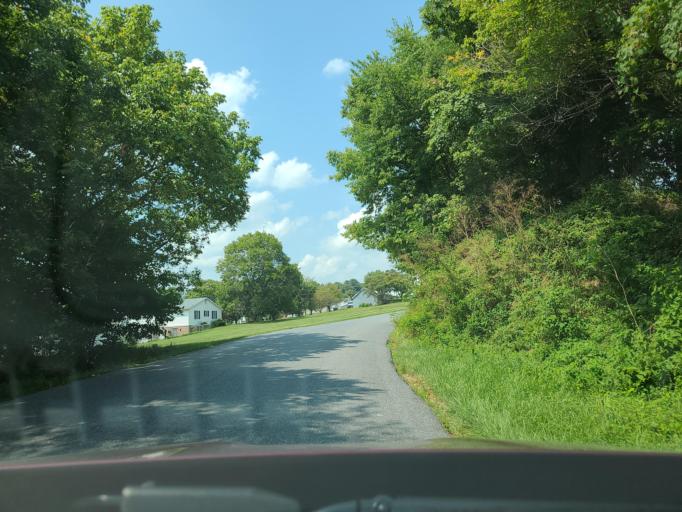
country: US
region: Maryland
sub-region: Frederick County
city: Linganore
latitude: 39.4827
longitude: -77.2464
